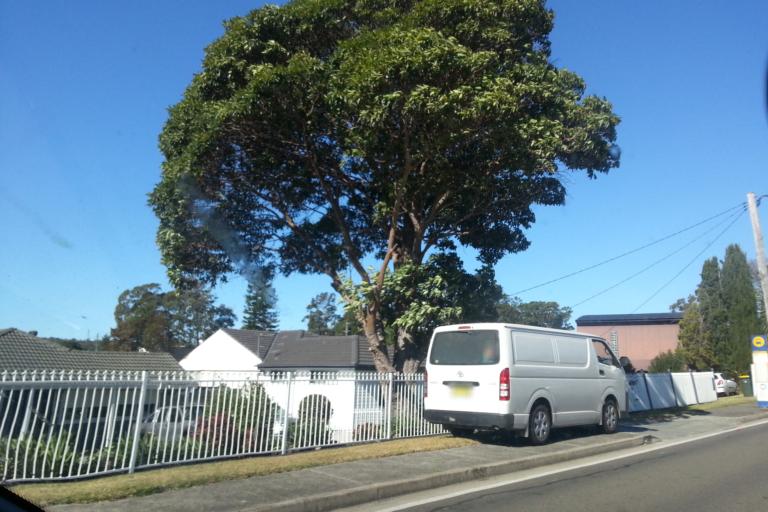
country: AU
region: New South Wales
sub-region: Wollongong
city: Dapto
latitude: -34.5067
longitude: 150.7862
